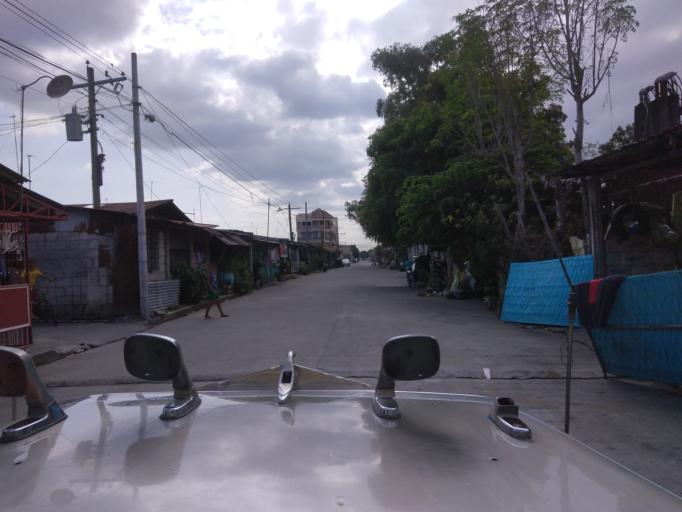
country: PH
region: Central Luzon
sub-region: Province of Pampanga
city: Pandacaqui
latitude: 15.1802
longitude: 120.6450
